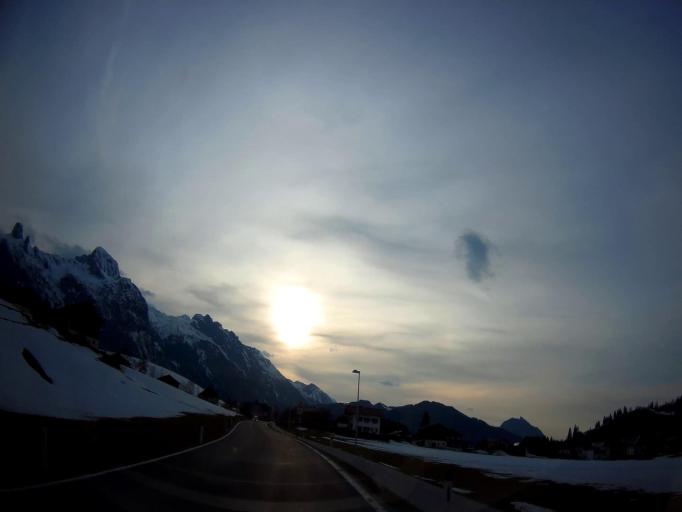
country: AT
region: Salzburg
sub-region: Politischer Bezirk Hallein
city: Abtenau
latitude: 47.5604
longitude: 13.3684
